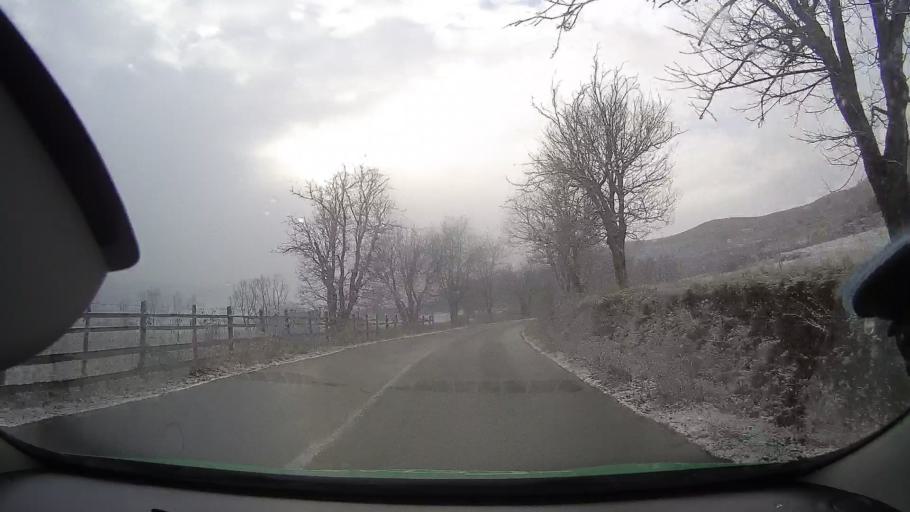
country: RO
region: Alba
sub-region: Comuna Rimetea
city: Rimetea
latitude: 46.4357
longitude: 23.5614
